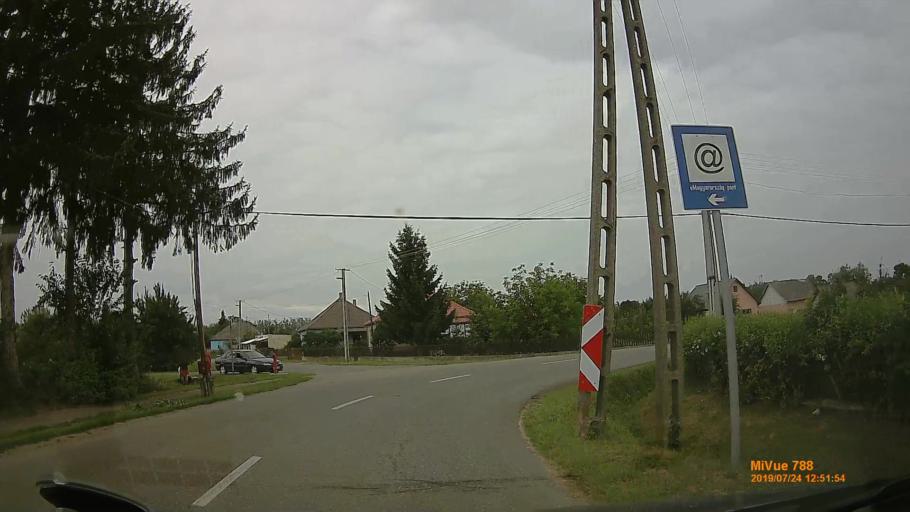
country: HU
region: Szabolcs-Szatmar-Bereg
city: Aranyosapati
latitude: 48.1949
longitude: 22.2958
